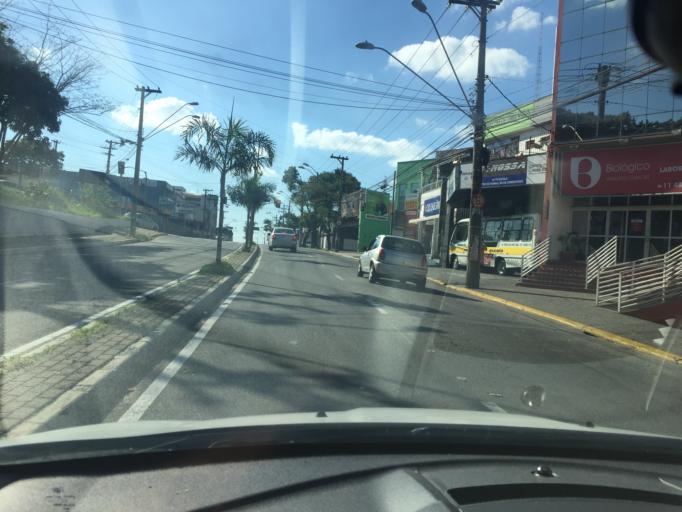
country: BR
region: Sao Paulo
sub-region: Varzea Paulista
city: Varzea Paulista
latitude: -23.2112
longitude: -46.8453
